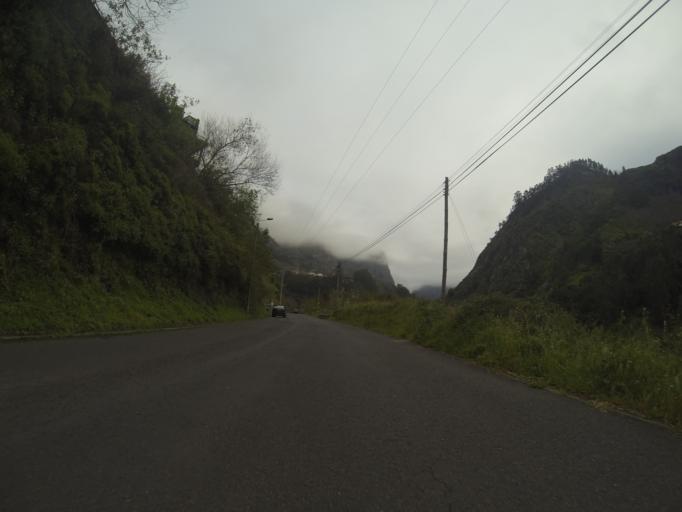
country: PT
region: Madeira
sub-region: Camara de Lobos
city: Curral das Freiras
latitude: 32.7265
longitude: -16.9659
